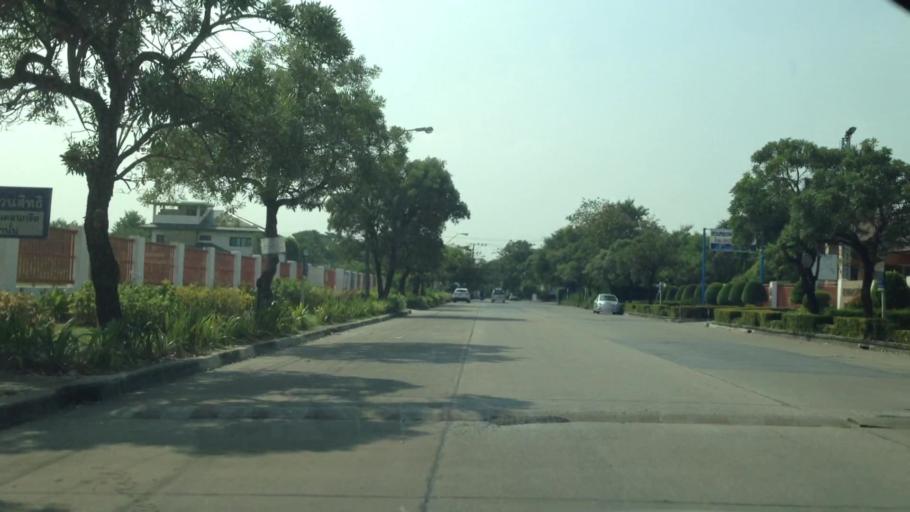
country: TH
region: Bangkok
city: Bang Na
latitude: 13.6872
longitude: 100.6578
